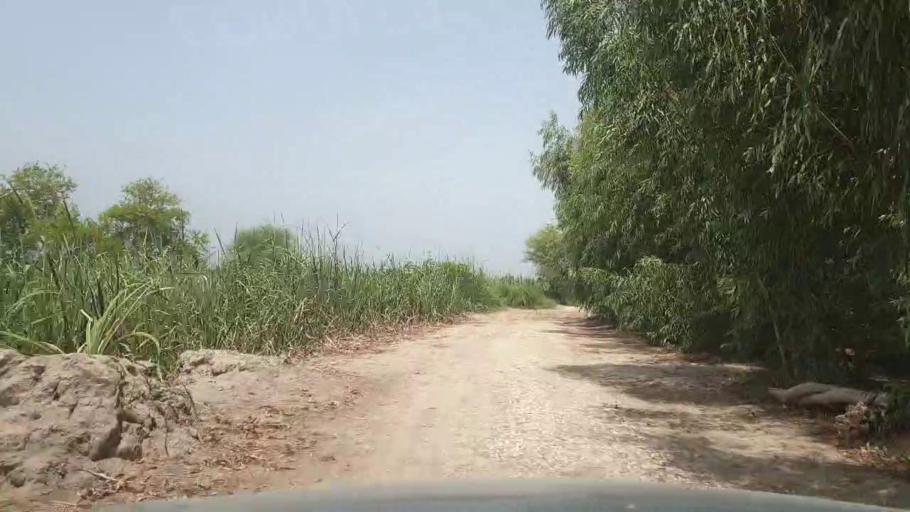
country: PK
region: Sindh
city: Garhi Yasin
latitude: 27.9464
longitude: 68.4293
